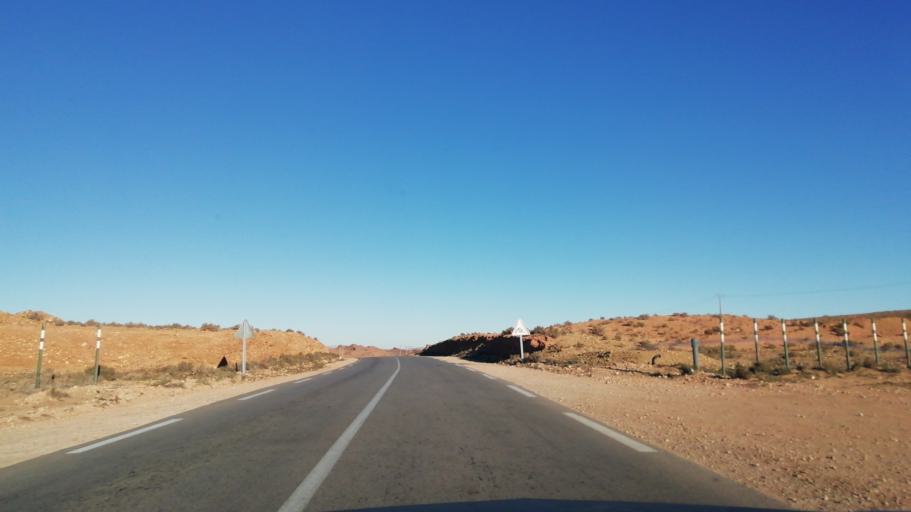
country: DZ
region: El Bayadh
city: El Abiodh Sidi Cheikh
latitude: 33.1727
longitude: 0.4429
